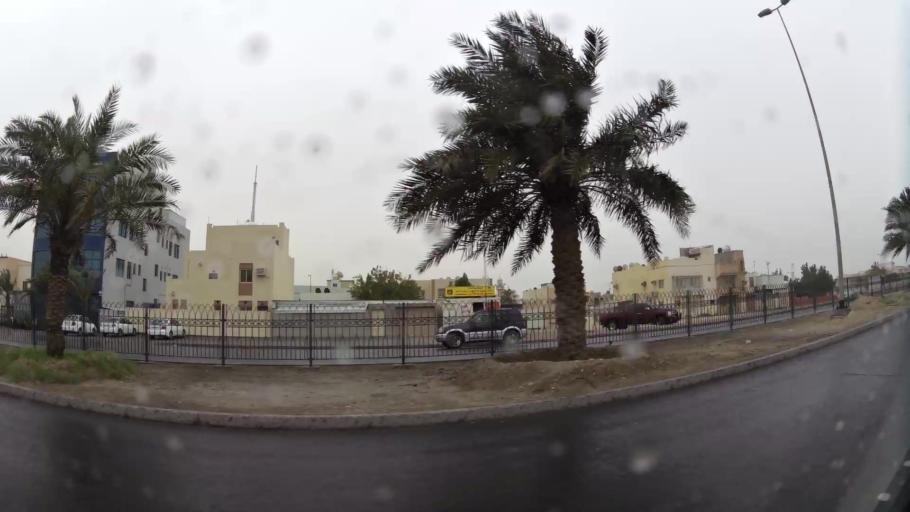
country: BH
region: Northern
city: Madinat `Isa
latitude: 26.1677
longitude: 50.5577
